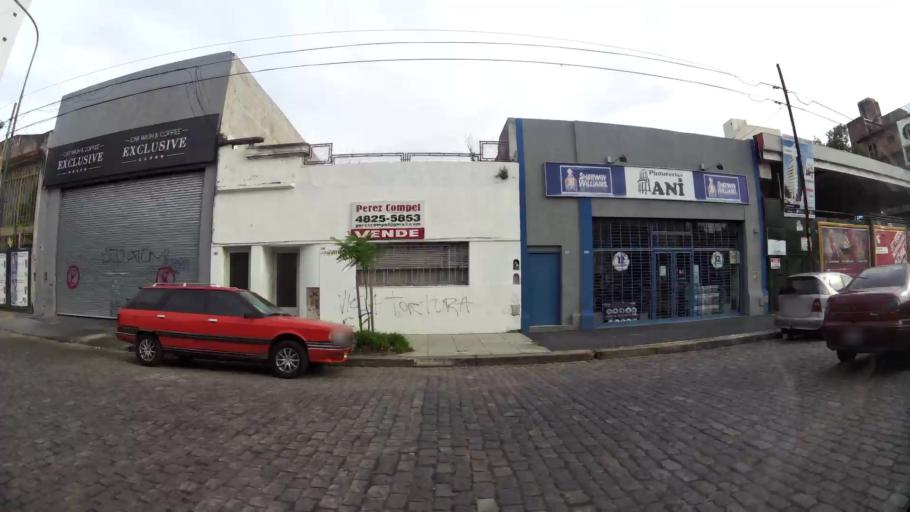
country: AR
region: Buenos Aires F.D.
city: Villa Santa Rita
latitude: -34.6357
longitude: -58.4750
